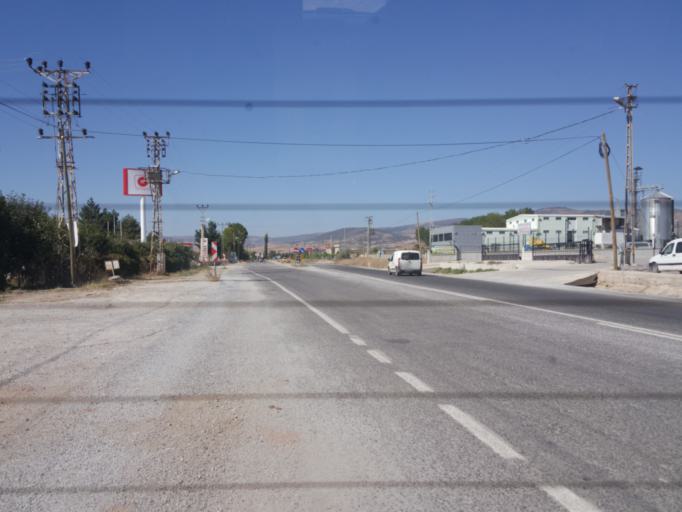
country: TR
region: Tokat
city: Zile
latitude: 40.3103
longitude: 35.9138
